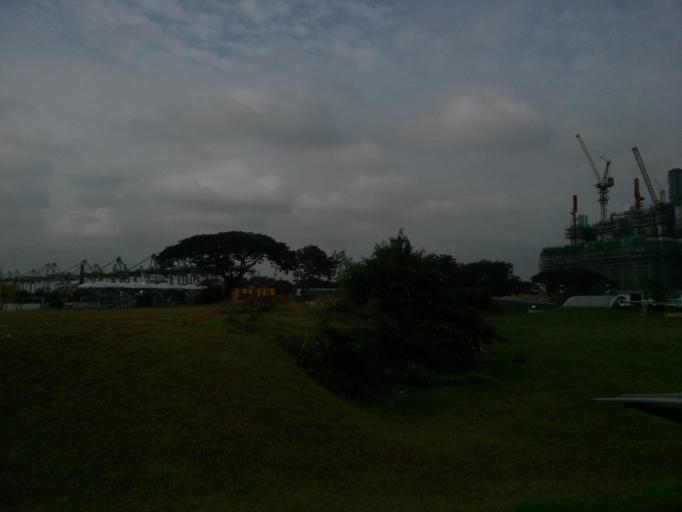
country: SG
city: Singapore
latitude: 1.2774
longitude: 103.8557
